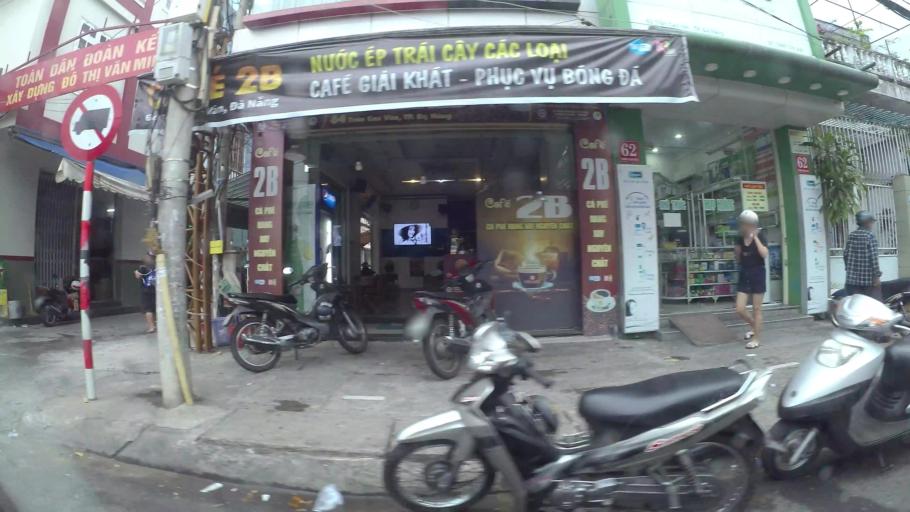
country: VN
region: Da Nang
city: Da Nang
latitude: 16.0731
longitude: 108.2111
